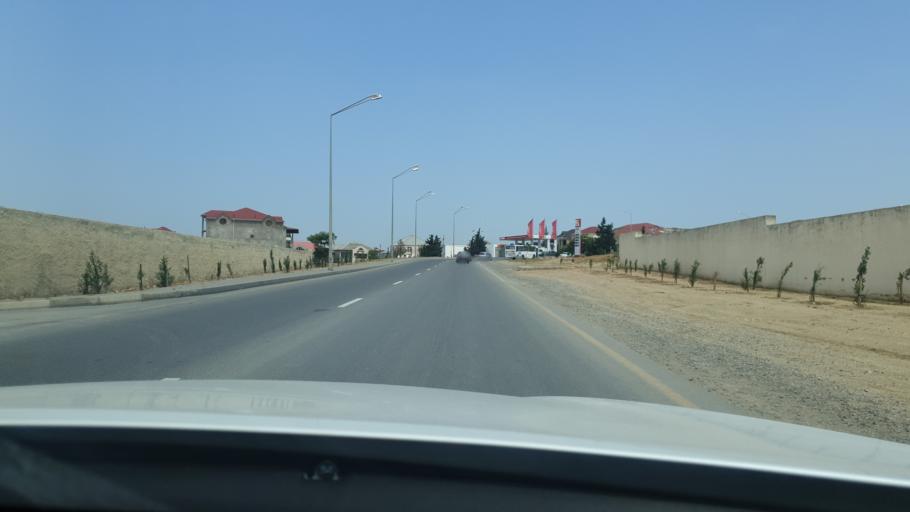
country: AZ
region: Baki
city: Qaracuxur
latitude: 40.3924
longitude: 49.9887
